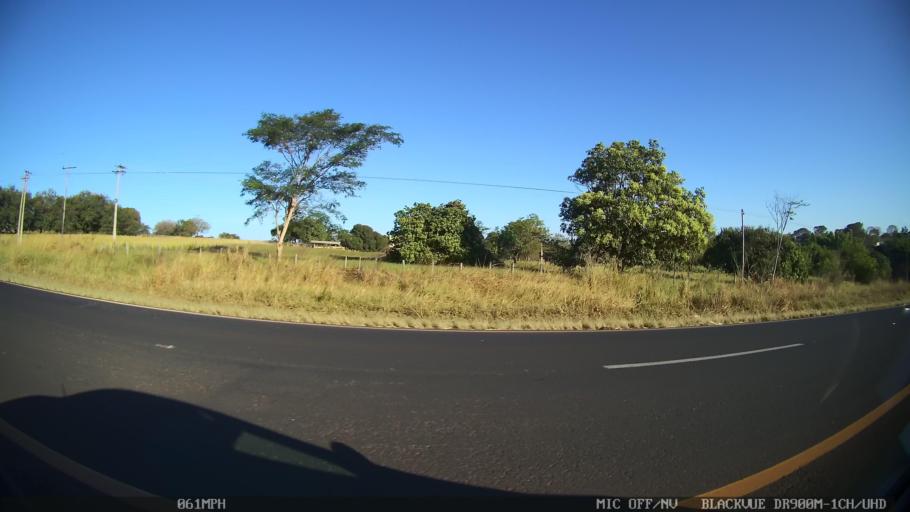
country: BR
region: Sao Paulo
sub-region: Guapiacu
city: Guapiacu
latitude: -20.7696
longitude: -49.2116
